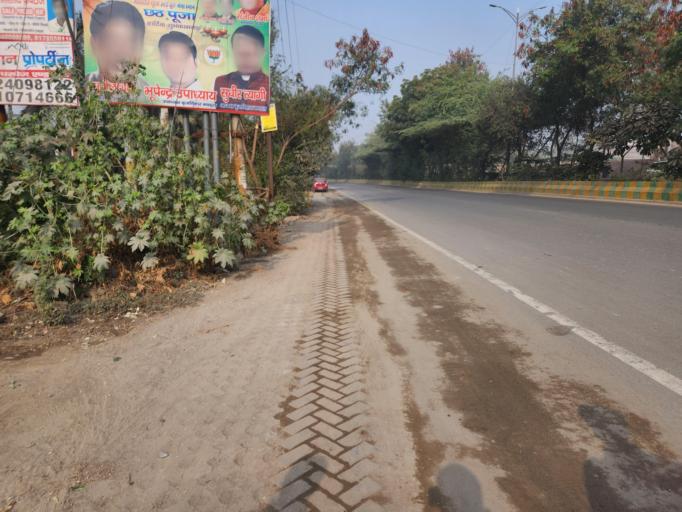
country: IN
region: Uttar Pradesh
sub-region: Ghaziabad
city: Ghaziabad
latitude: 28.6687
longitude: 77.3695
